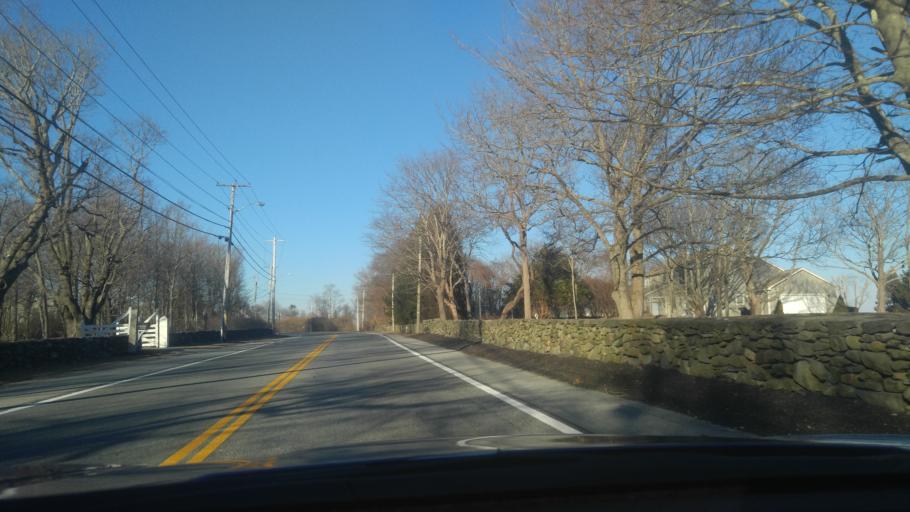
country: US
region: Rhode Island
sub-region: Washington County
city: Narragansett Pier
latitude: 41.4615
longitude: -71.4334
